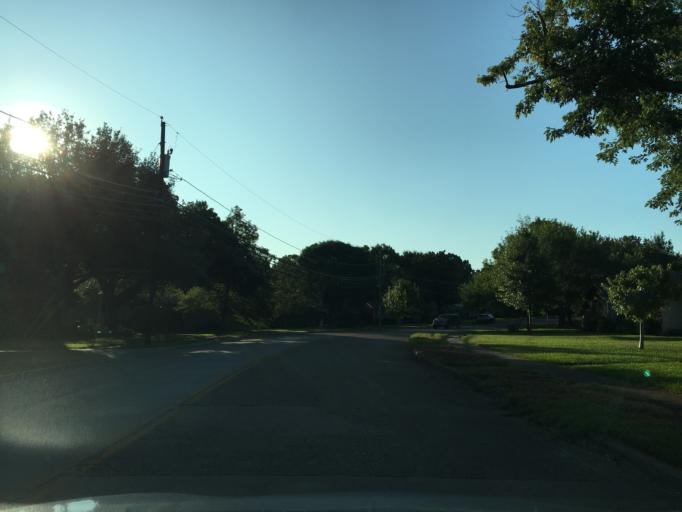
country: US
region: Texas
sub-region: Dallas County
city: Highland Park
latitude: 32.8630
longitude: -96.7394
